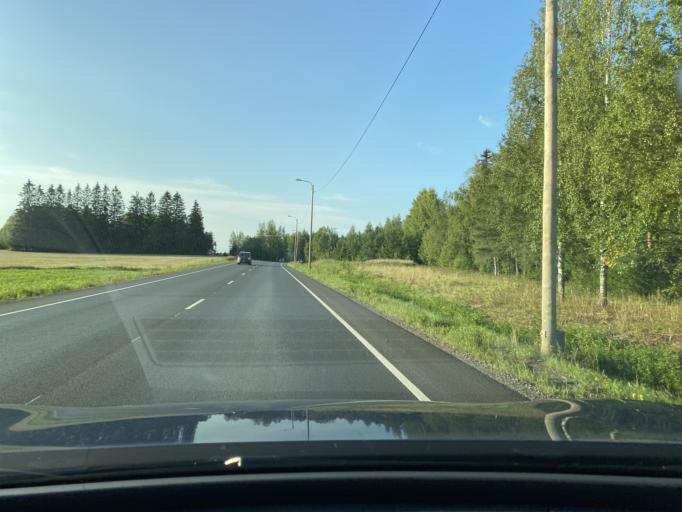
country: FI
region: Kymenlaakso
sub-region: Kouvola
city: Kouvola
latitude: 60.8783
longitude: 26.6024
